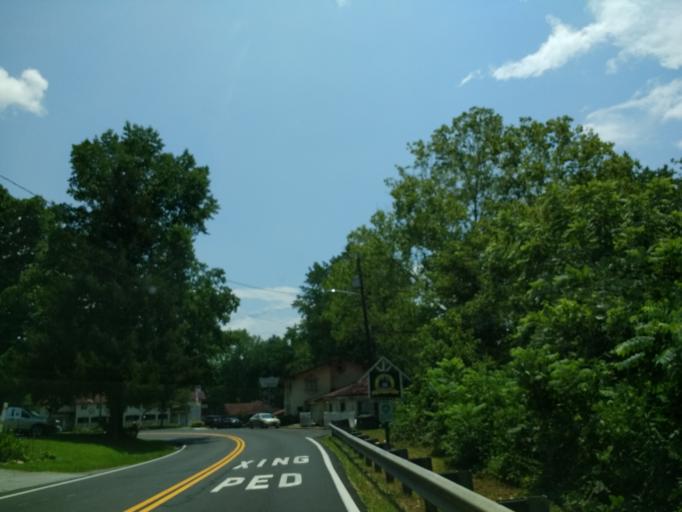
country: US
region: Georgia
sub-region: White County
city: Cleveland
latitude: 34.7030
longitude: -83.7369
